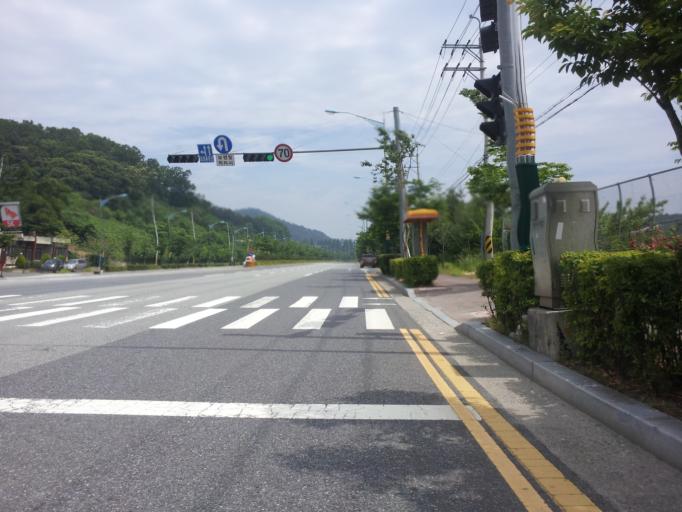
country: KR
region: Daejeon
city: Daejeon
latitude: 36.3256
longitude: 127.4733
